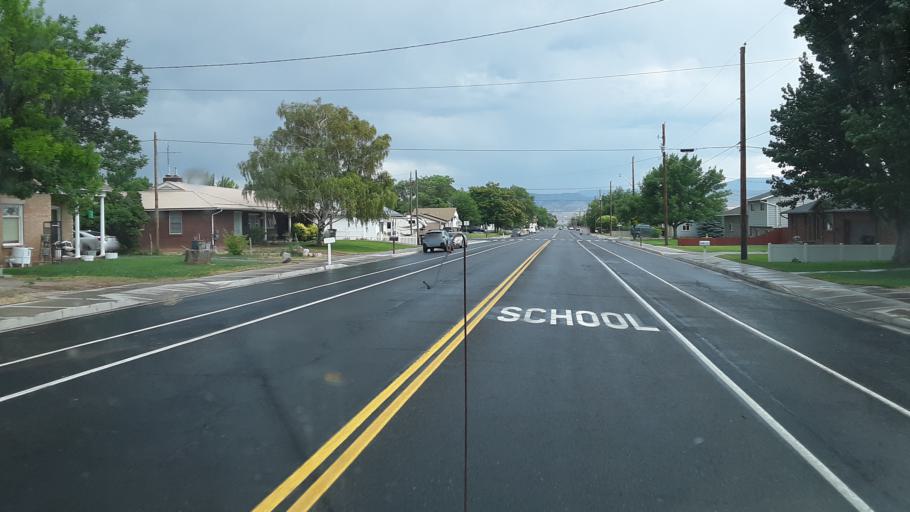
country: US
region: Utah
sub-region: Sevier County
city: Richfield
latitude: 38.7723
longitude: -112.0898
